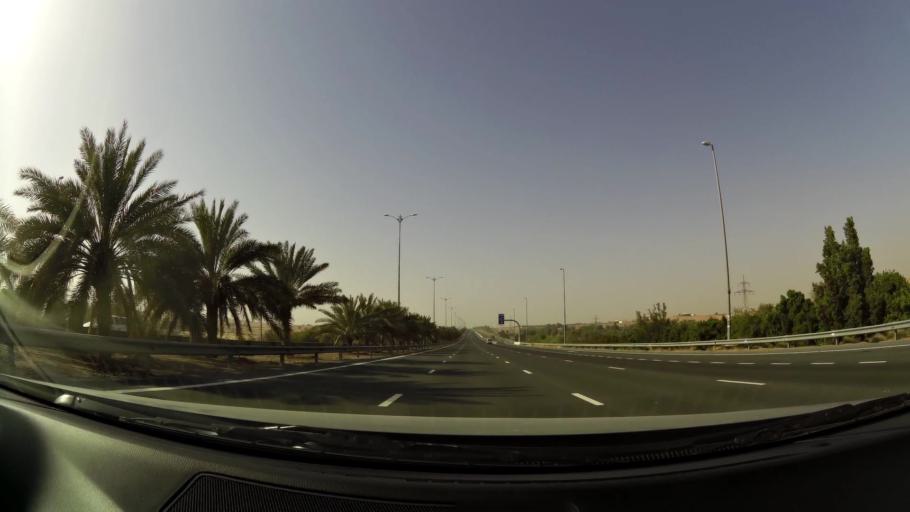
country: OM
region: Al Buraimi
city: Al Buraymi
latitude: 24.5538
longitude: 55.7539
